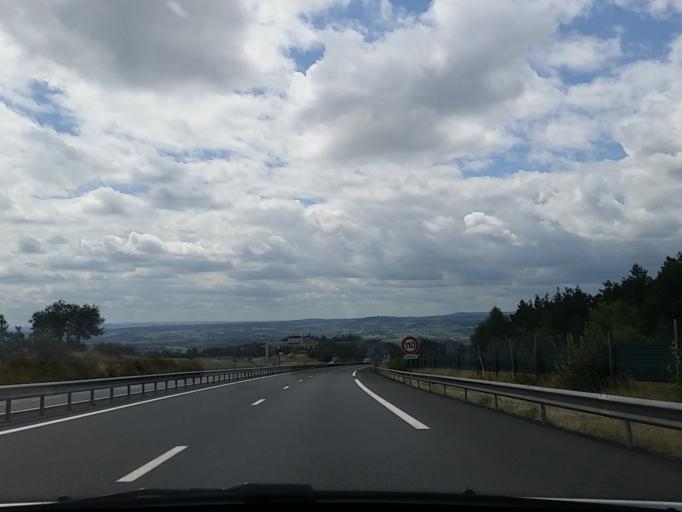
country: FR
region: Auvergne
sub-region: Departement du Cantal
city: Saint-Flour
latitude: 45.0926
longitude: 3.1236
